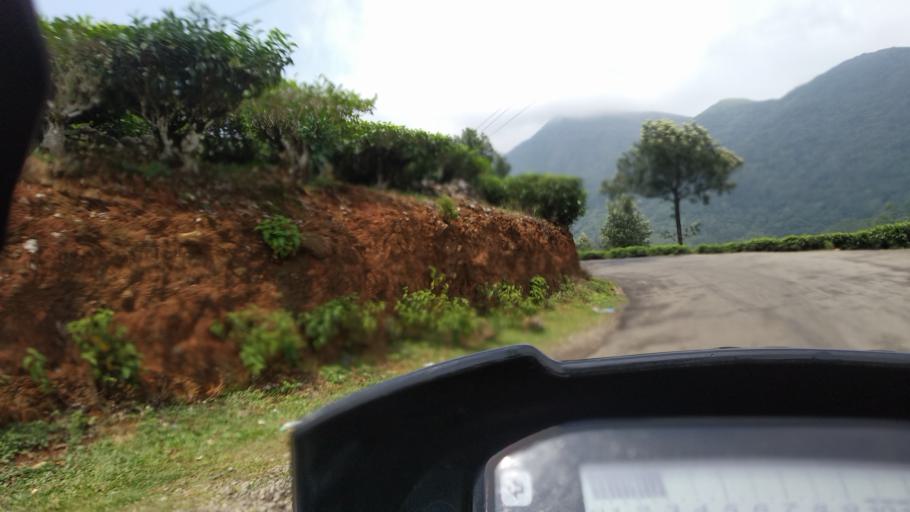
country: IN
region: Kerala
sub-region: Kottayam
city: Erattupetta
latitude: 9.6261
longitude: 76.9681
